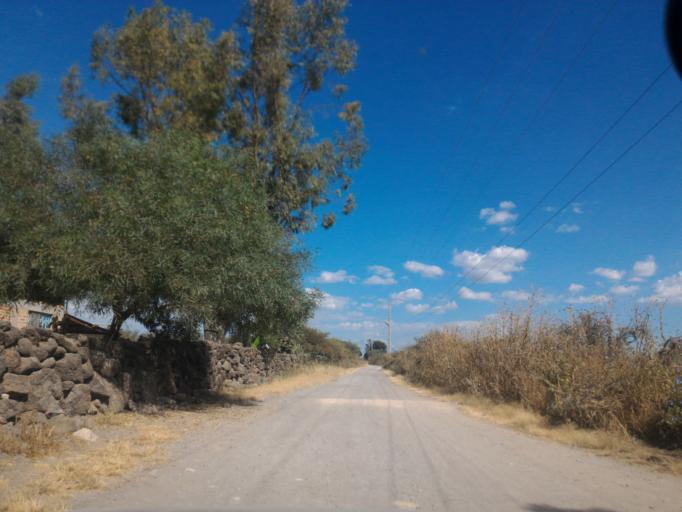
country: MX
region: Jalisco
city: San Diego de Alejandria
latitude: 20.8821
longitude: -102.0106
